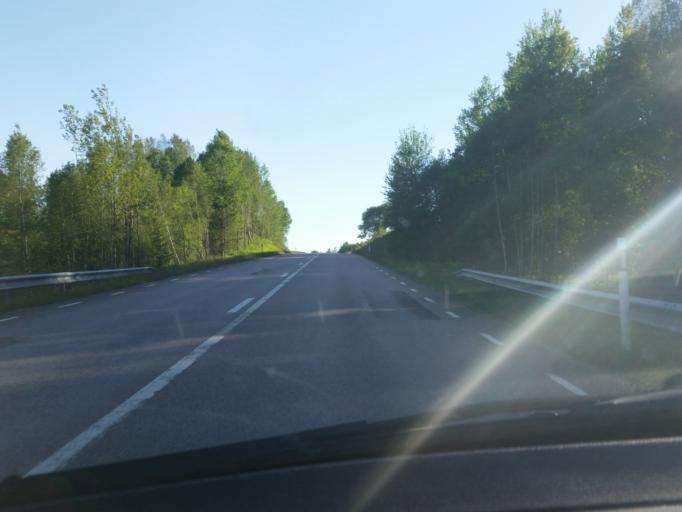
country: SE
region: Vaestra Goetaland
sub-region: Fargelanda Kommun
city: Faergelanda
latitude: 58.5776
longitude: 12.0123
